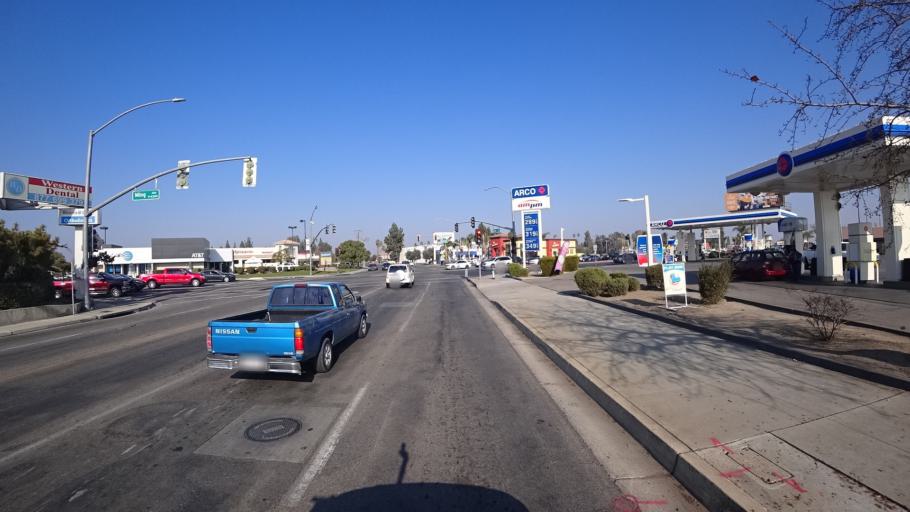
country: US
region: California
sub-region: Kern County
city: Bakersfield
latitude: 35.3392
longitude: -119.0506
